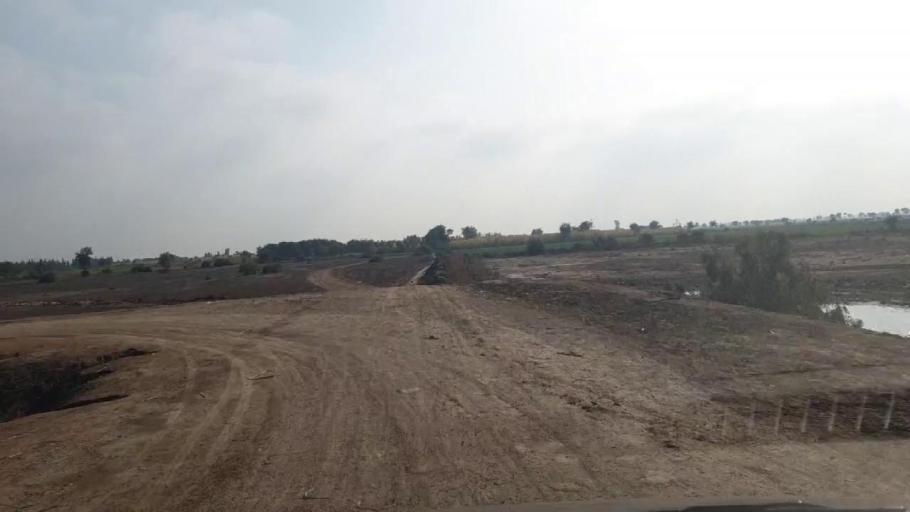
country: PK
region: Sindh
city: Shahdadpur
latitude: 25.9119
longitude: 68.6827
